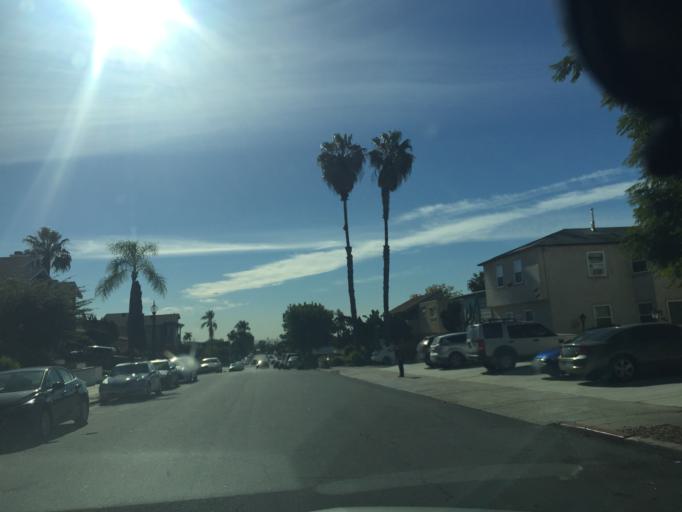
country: US
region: California
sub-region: San Diego County
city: Lemon Grove
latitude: 32.7581
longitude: -117.0890
